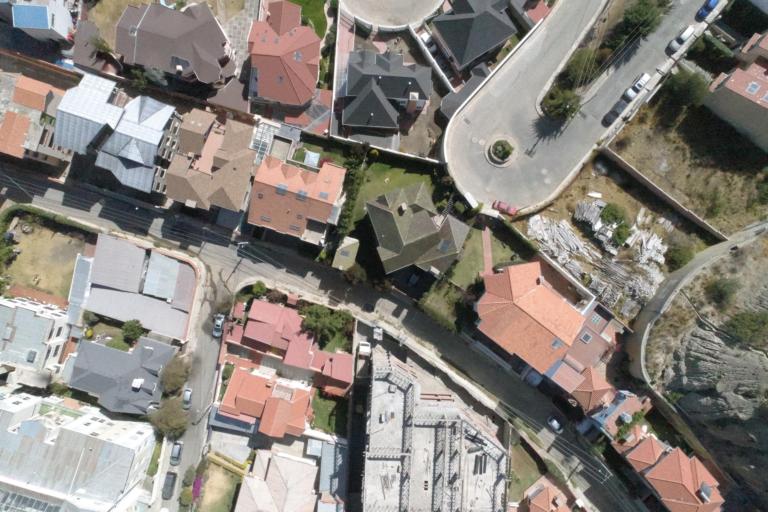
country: BO
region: La Paz
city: La Paz
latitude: -16.5348
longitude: -68.0710
